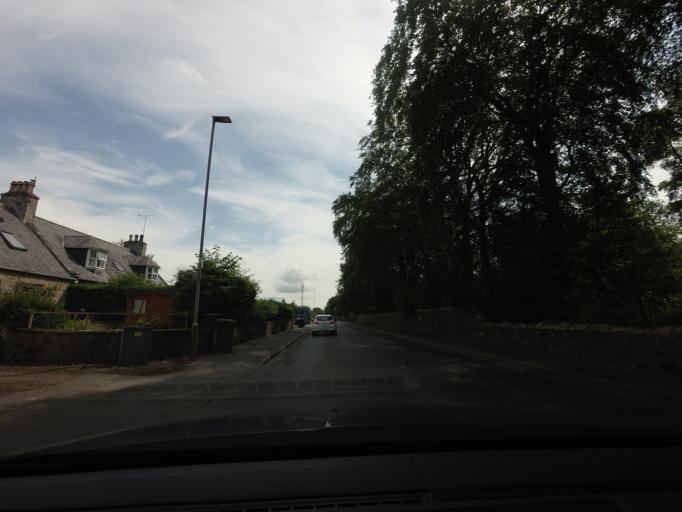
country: GB
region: Scotland
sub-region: Aberdeenshire
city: Mintlaw
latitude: 57.5259
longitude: -2.0183
